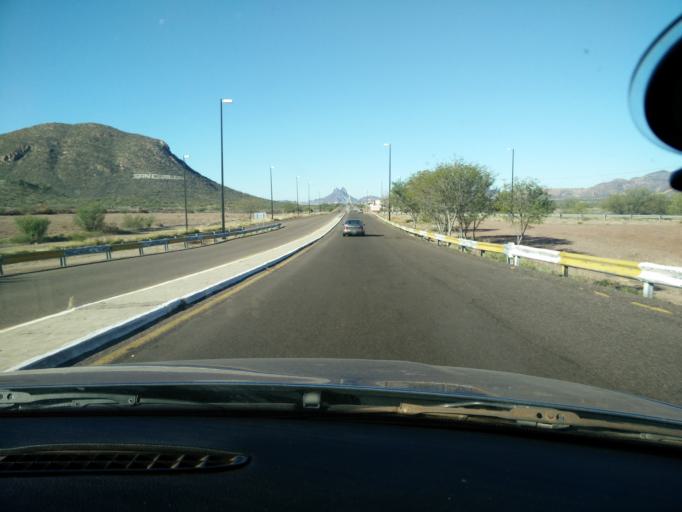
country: MX
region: Sonora
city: Heroica Guaymas
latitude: 27.9874
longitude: -110.9421
